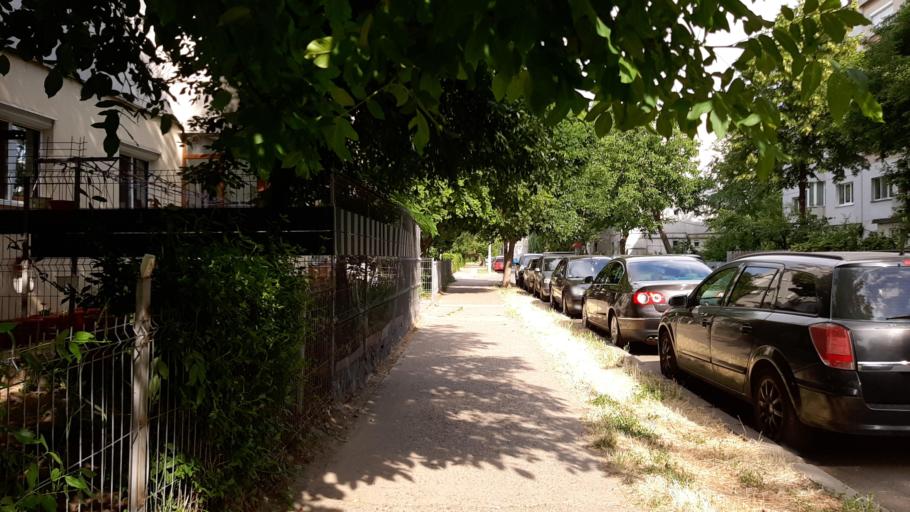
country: RO
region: Galati
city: Galati
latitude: 45.4435
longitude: 28.0256
